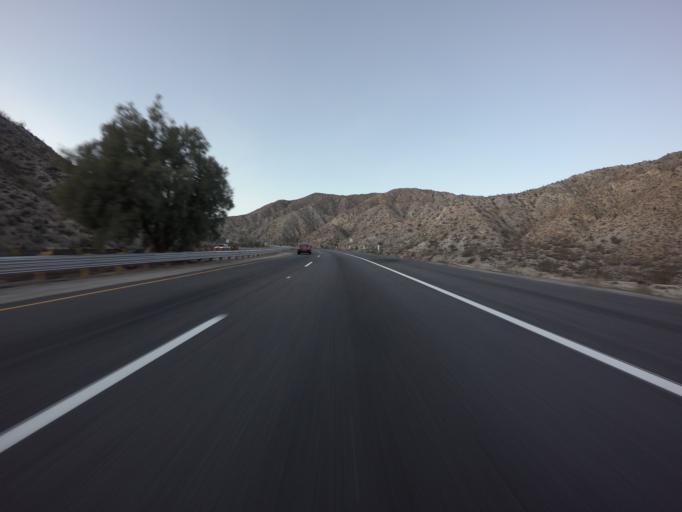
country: US
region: California
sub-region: San Bernardino County
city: Morongo Valley
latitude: 34.0163
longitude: -116.5803
